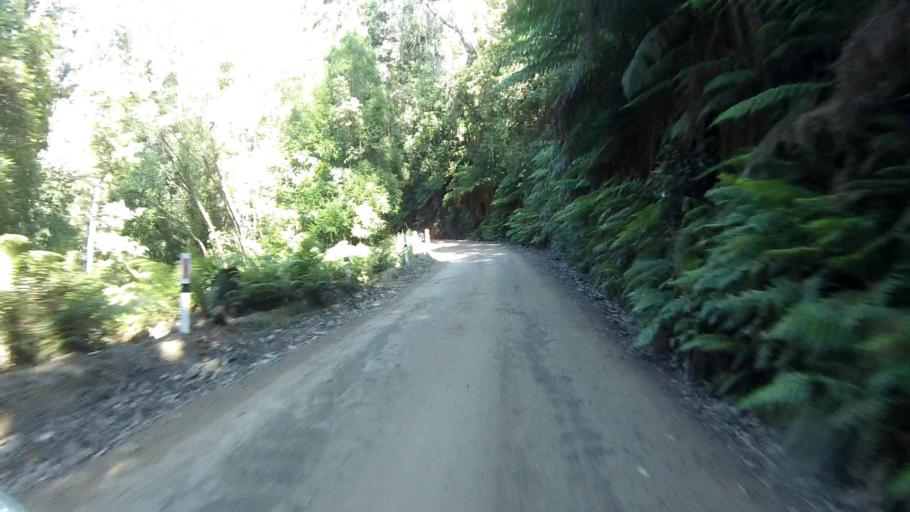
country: AU
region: Tasmania
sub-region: Derwent Valley
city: New Norfolk
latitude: -42.6780
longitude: 146.6896
